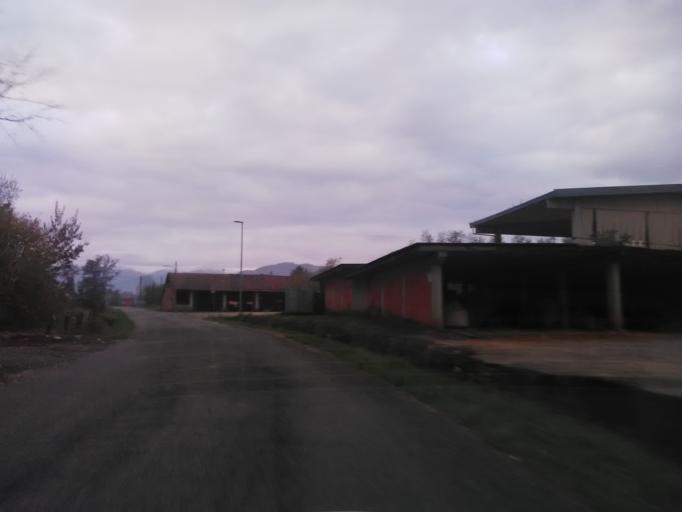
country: IT
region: Piedmont
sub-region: Provincia di Novara
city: Prato Sesia
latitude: 45.6647
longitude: 8.3712
